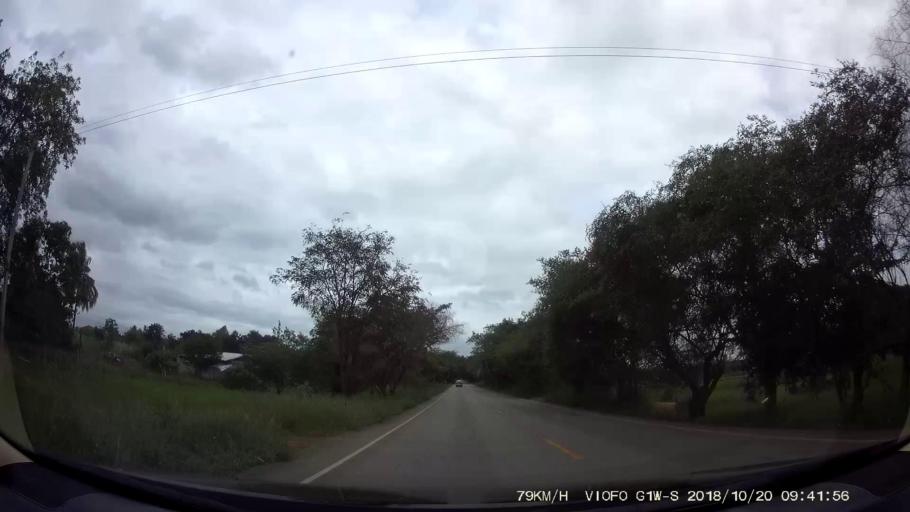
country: TH
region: Chaiyaphum
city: Khon San
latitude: 16.4584
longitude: 101.9547
